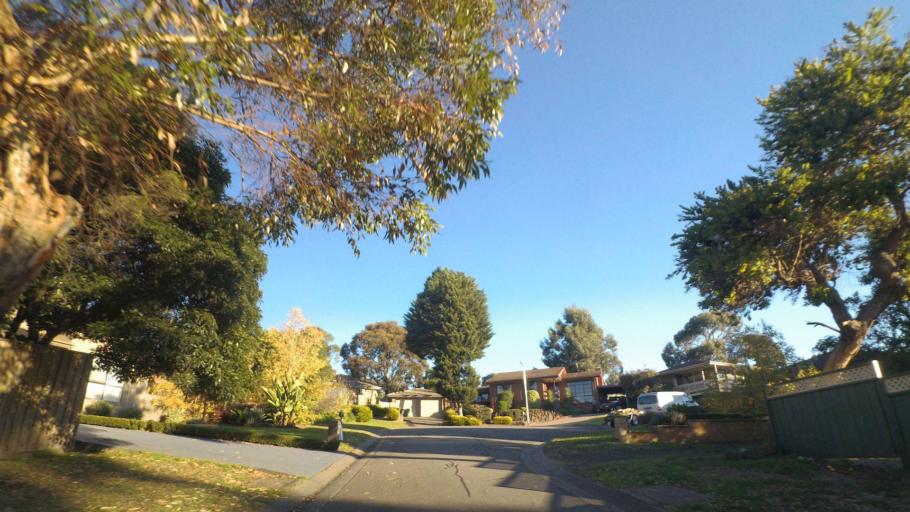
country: AU
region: Victoria
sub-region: Banyule
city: Greensborough
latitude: -37.6861
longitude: 145.1102
